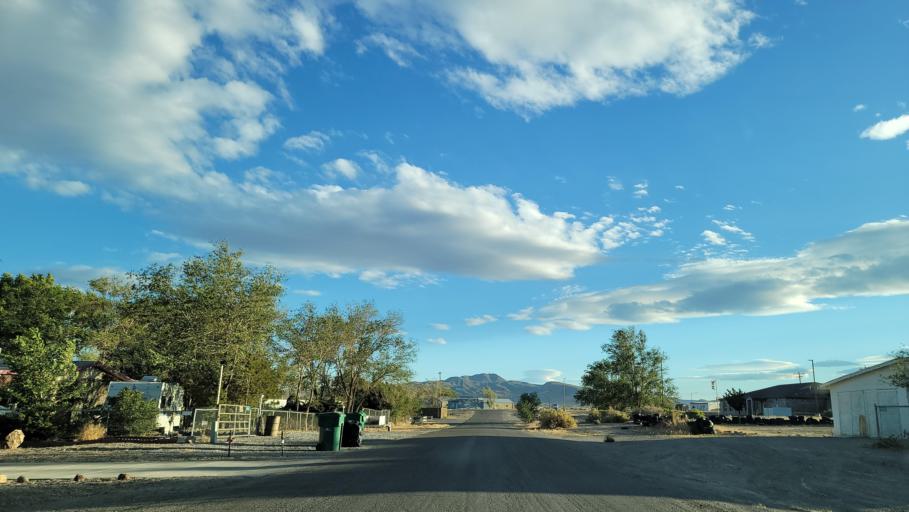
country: US
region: Nevada
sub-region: Lyon County
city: Silver Springs
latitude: 39.4157
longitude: -119.2223
